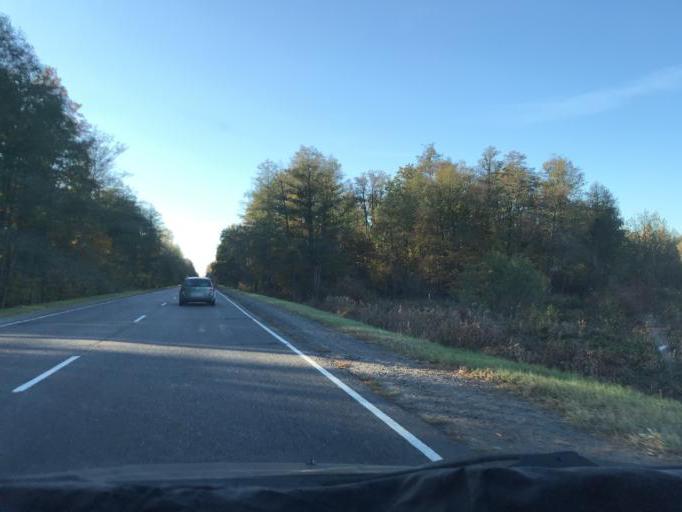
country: BY
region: Gomel
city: Pyetrykaw
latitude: 52.2645
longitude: 28.3083
